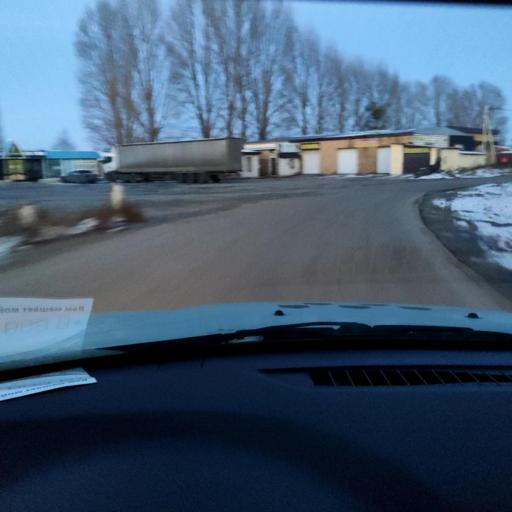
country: RU
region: Samara
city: Tol'yatti
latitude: 53.5693
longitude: 49.3911
